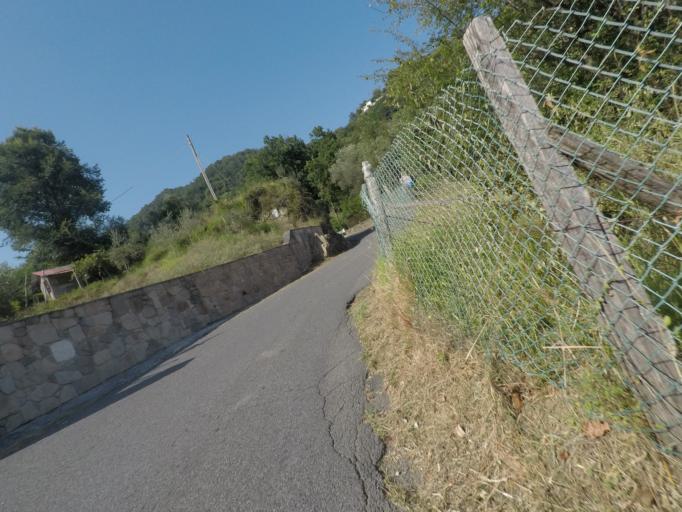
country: IT
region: Tuscany
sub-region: Provincia di Massa-Carrara
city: Carrara
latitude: 44.0771
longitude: 10.0740
